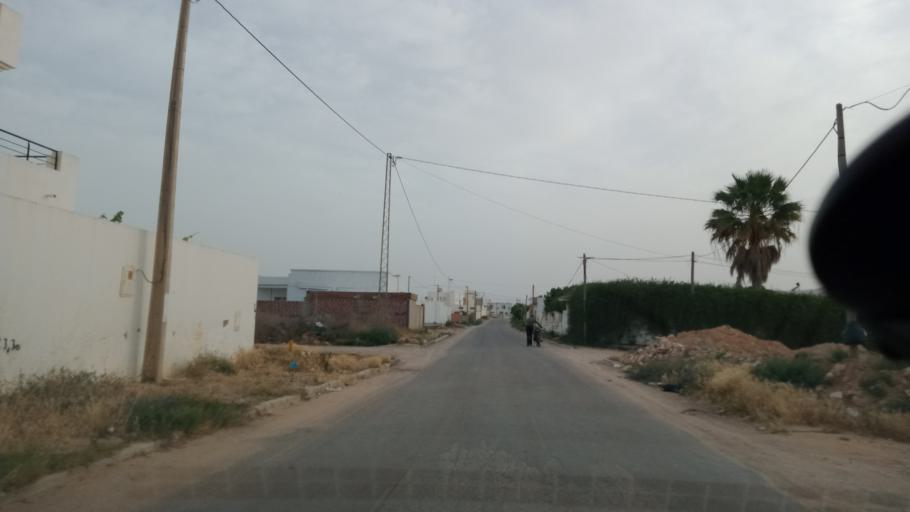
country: TN
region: Safaqis
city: Al Qarmadah
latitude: 34.7871
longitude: 10.7704
